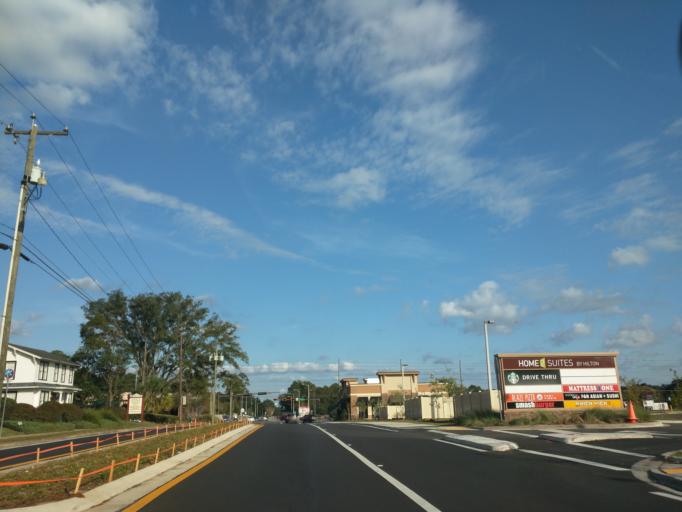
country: US
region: Florida
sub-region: Leon County
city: Tallahassee
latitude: 30.4417
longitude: -84.2634
